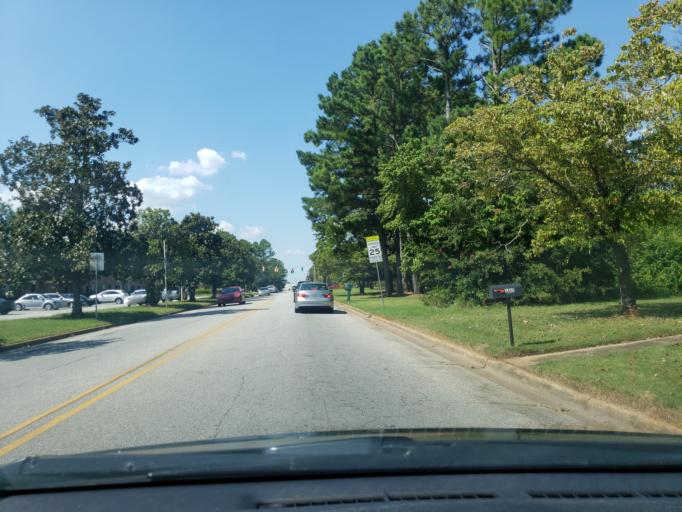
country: US
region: Georgia
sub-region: Dougherty County
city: Albany
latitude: 31.6108
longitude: -84.2042
